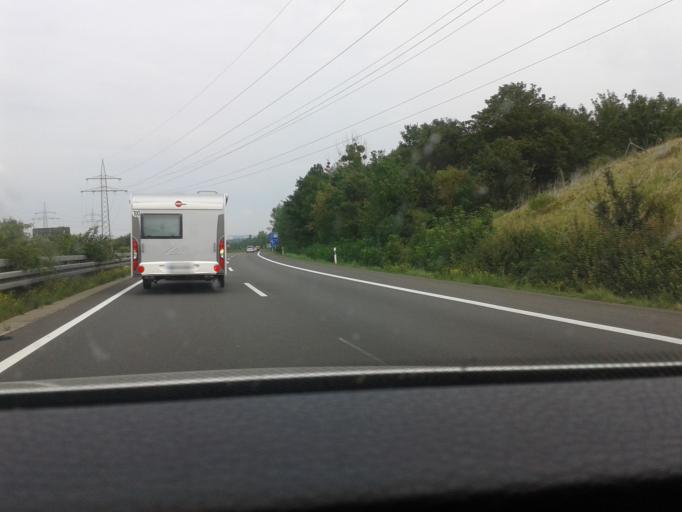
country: DE
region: Lower Saxony
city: Wolfsburg
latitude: 52.4058
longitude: 10.7319
